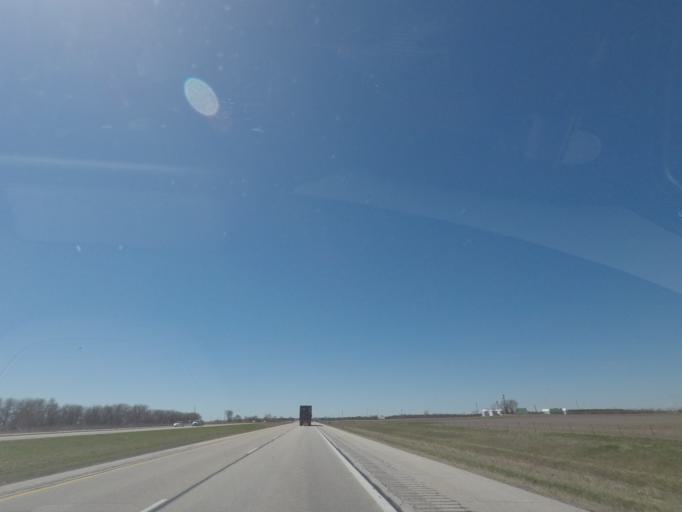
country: US
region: Illinois
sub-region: McLean County
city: Lexington
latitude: 40.6127
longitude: -88.8284
